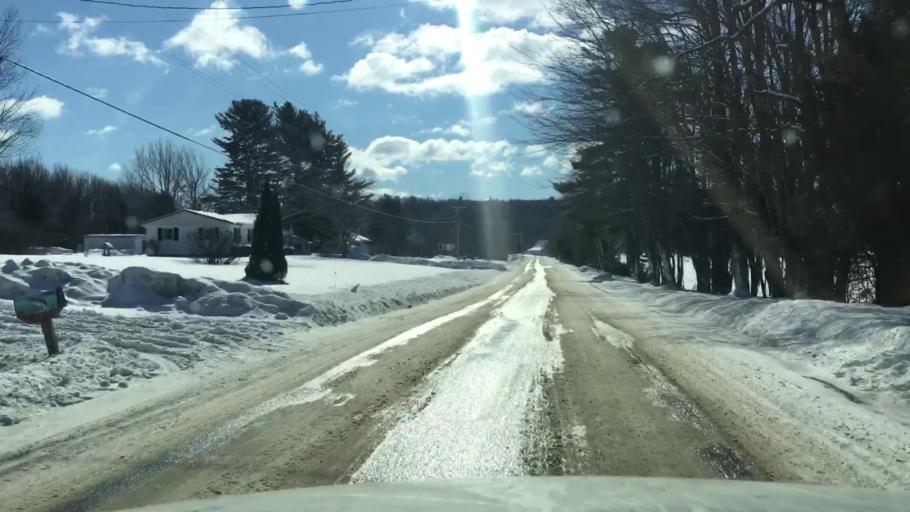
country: US
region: Maine
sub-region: Washington County
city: Calais
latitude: 45.0665
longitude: -67.4731
